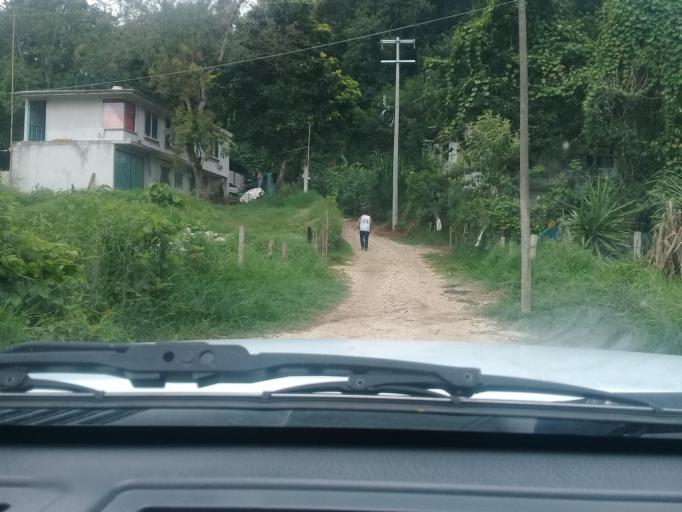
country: MX
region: Veracruz
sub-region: Tlalnelhuayocan
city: Otilpan
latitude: 19.5544
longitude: -96.9793
